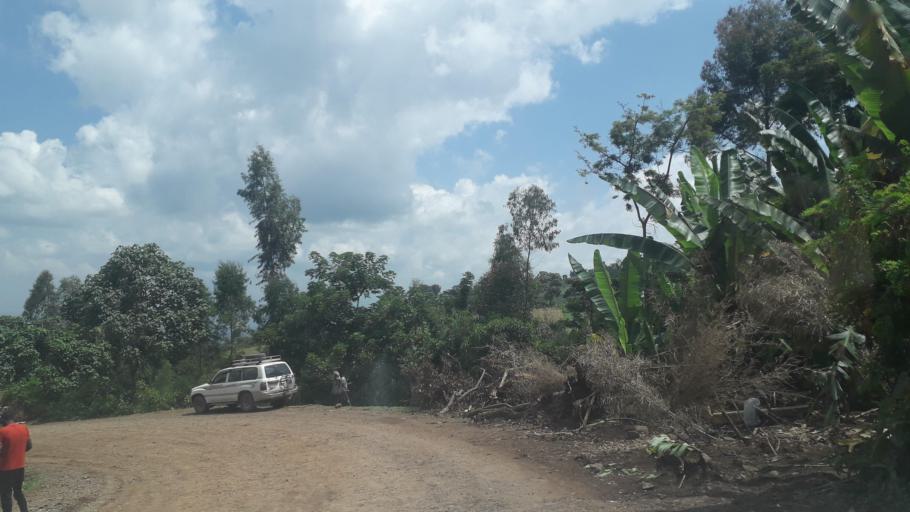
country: ET
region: Oromiya
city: Jima
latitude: 7.4659
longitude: 36.8759
